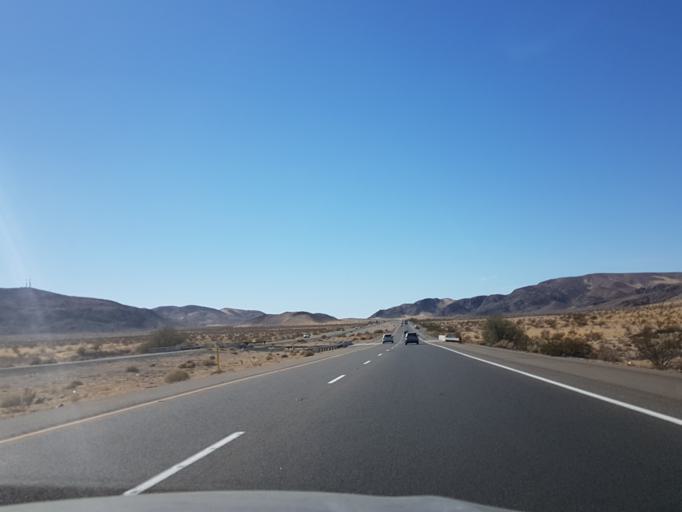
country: US
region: California
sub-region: San Bernardino County
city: Fort Irwin
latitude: 35.0870
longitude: -116.3495
